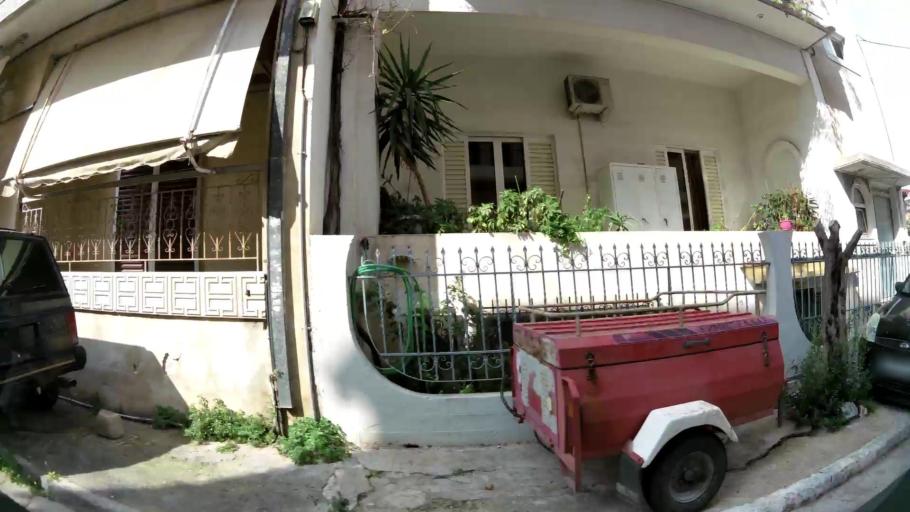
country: GR
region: Attica
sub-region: Nomarchia Athinas
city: Petroupolis
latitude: 38.0466
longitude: 23.6898
